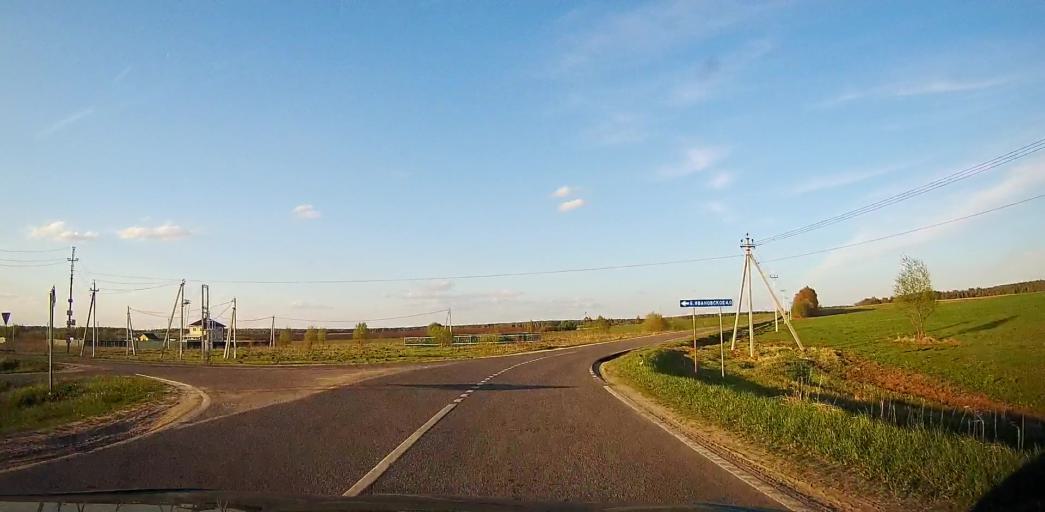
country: RU
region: Moskovskaya
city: Bronnitsy
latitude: 55.2822
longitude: 38.1733
